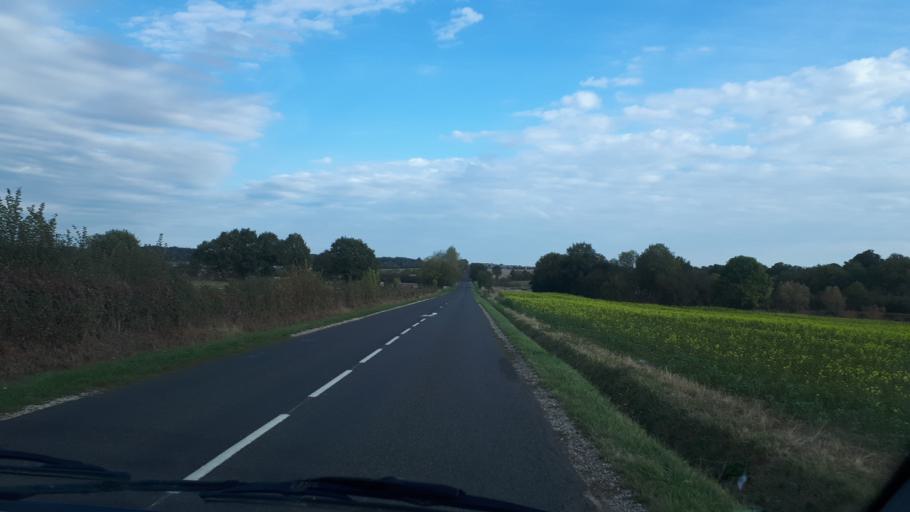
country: FR
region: Centre
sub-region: Departement du Loir-et-Cher
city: Mondoubleau
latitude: 47.9164
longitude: 0.9316
